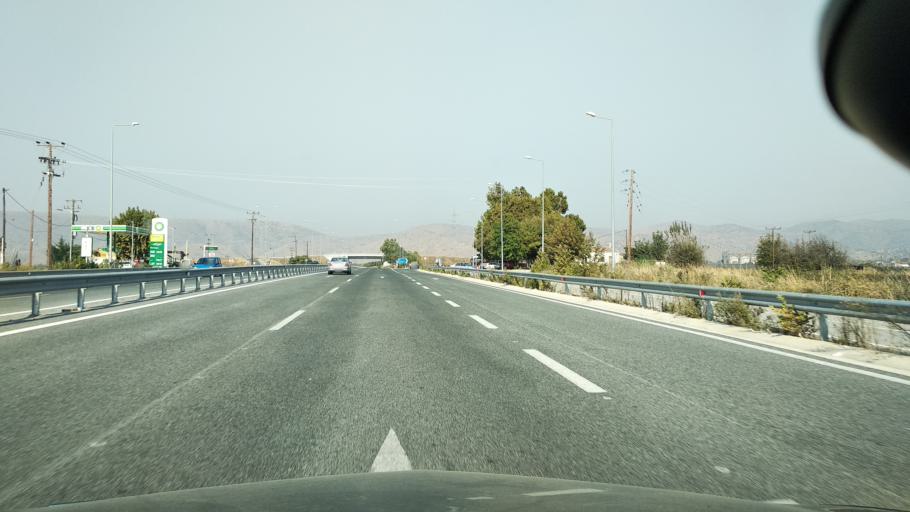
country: GR
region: Thessaly
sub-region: Trikala
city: Zarkos
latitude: 39.5912
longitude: 22.1280
